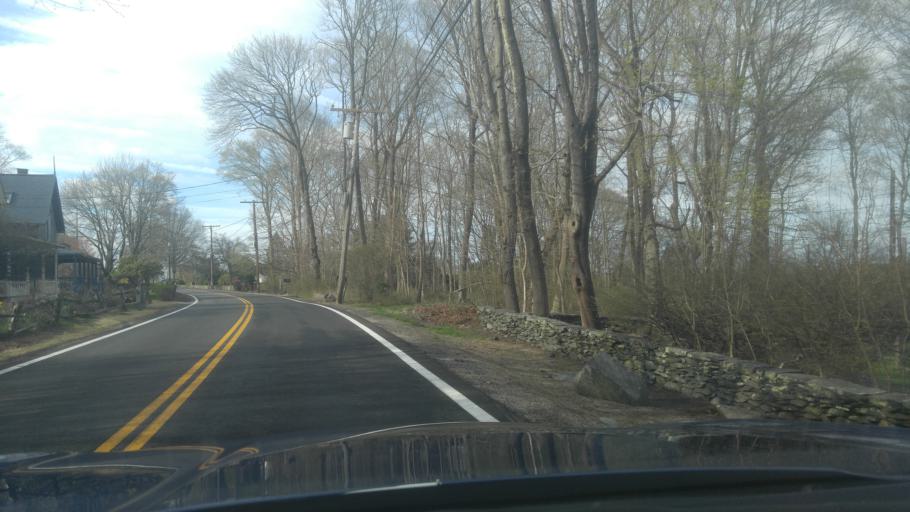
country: US
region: Rhode Island
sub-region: Newport County
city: Jamestown
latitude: 41.5680
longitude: -71.3650
